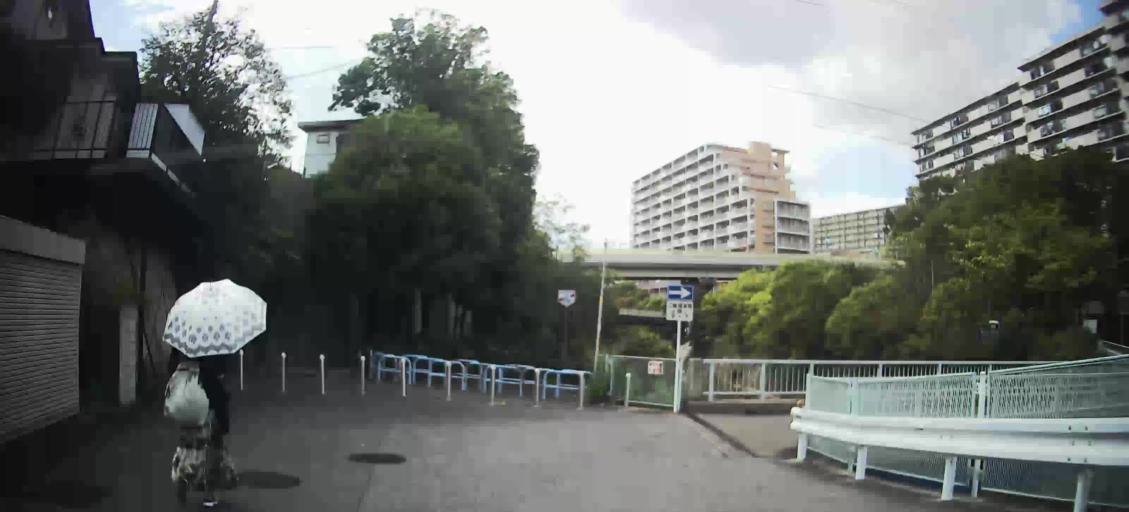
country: JP
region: Kanagawa
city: Minami-rinkan
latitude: 35.4770
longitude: 139.5483
